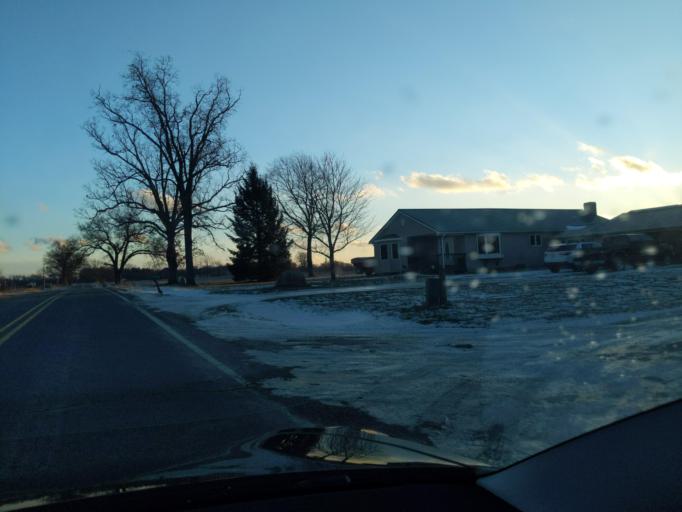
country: US
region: Michigan
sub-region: Ingham County
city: Stockbridge
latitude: 42.4509
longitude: -84.2098
